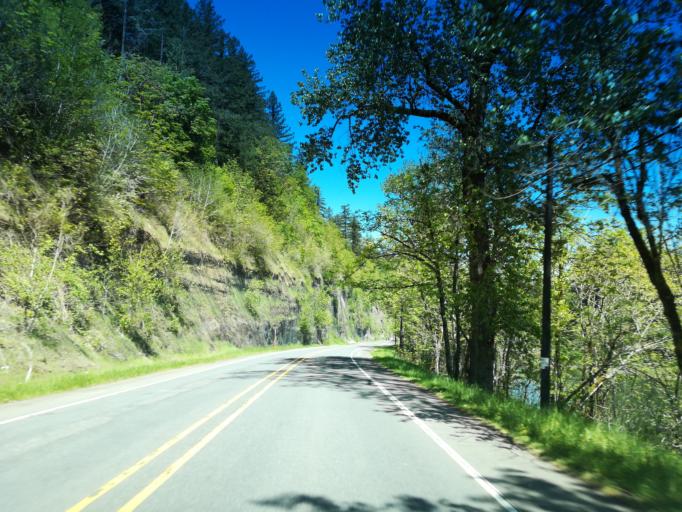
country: US
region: Oregon
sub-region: Multnomah County
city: Troutdale
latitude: 45.5138
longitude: -122.3645
